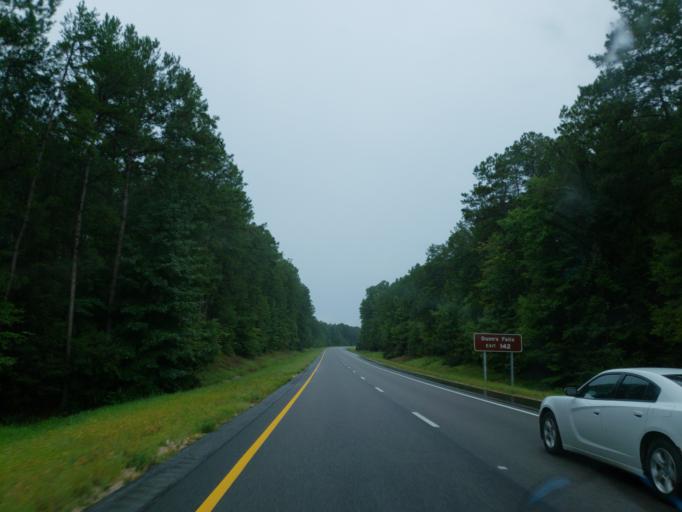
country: US
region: Mississippi
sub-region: Lauderdale County
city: Nellieburg
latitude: 32.2767
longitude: -88.8045
